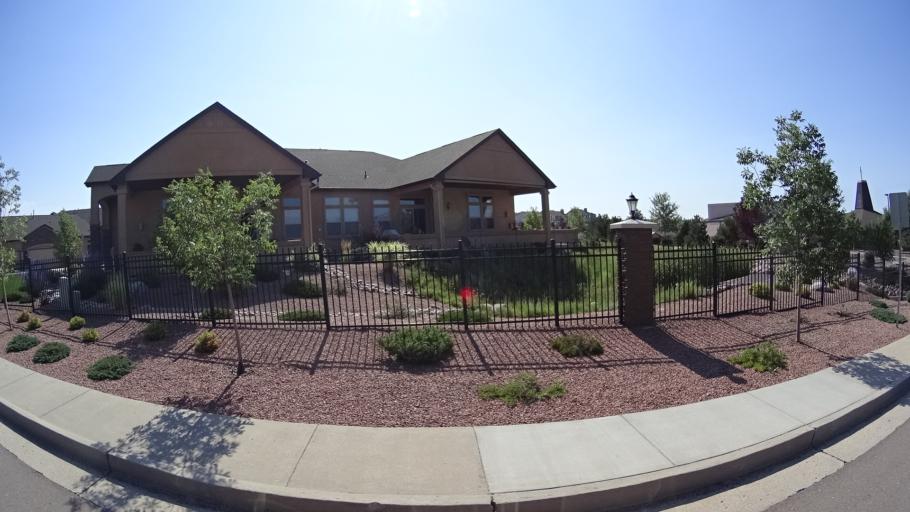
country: US
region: Colorado
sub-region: El Paso County
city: Air Force Academy
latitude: 38.9538
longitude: -104.7886
